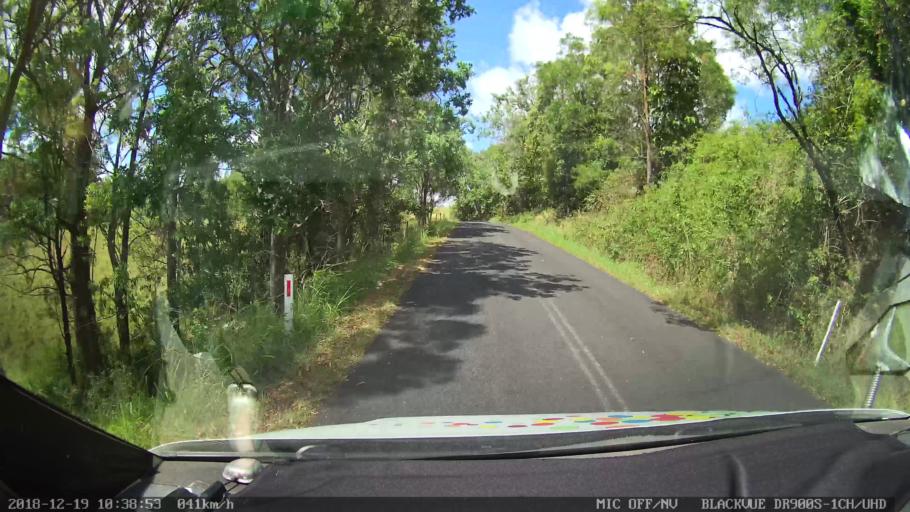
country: AU
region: New South Wales
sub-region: Lismore Municipality
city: Nimbin
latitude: -28.5774
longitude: 153.1551
